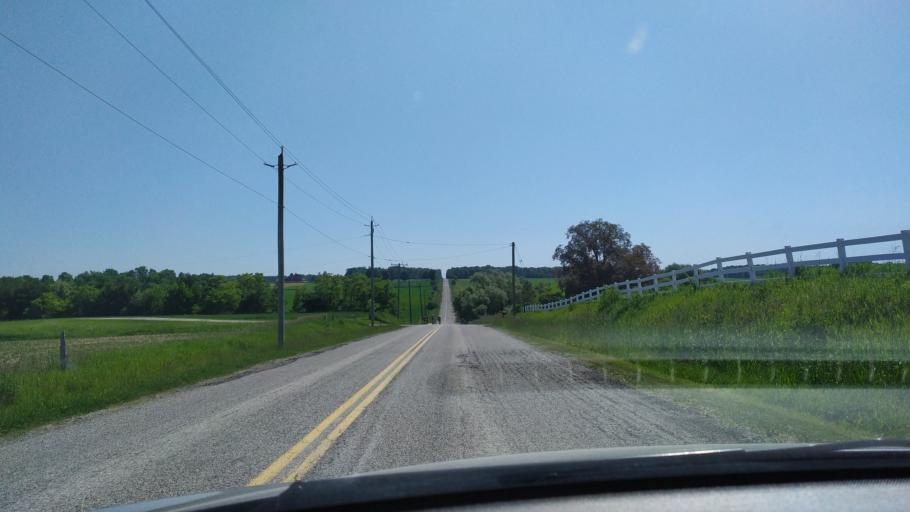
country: CA
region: Ontario
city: Waterloo
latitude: 43.4555
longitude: -80.7415
